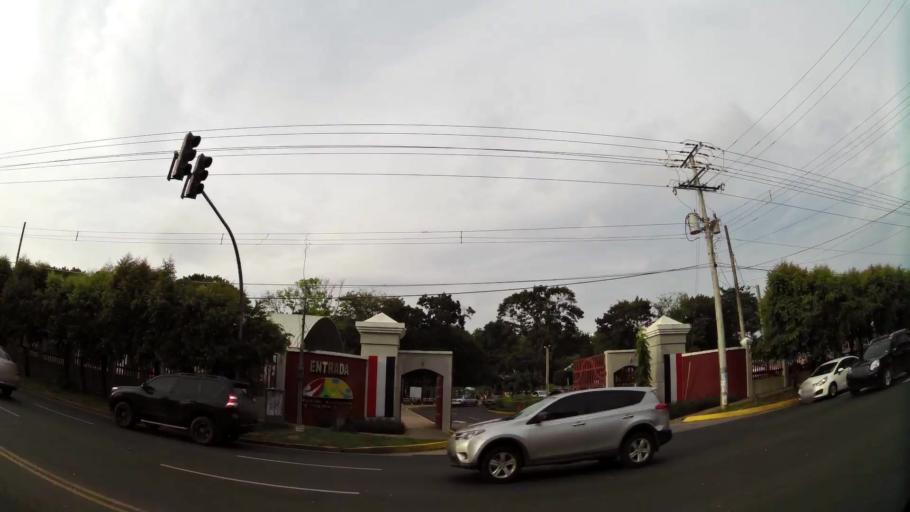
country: PA
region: Panama
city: Panama
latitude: 8.9971
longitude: -79.5077
